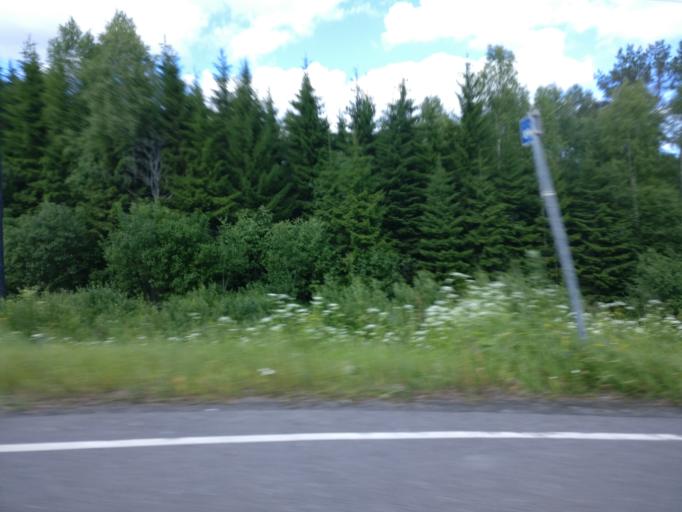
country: FI
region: Southern Savonia
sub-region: Savonlinna
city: Kerimaeki
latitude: 61.8631
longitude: 29.1452
